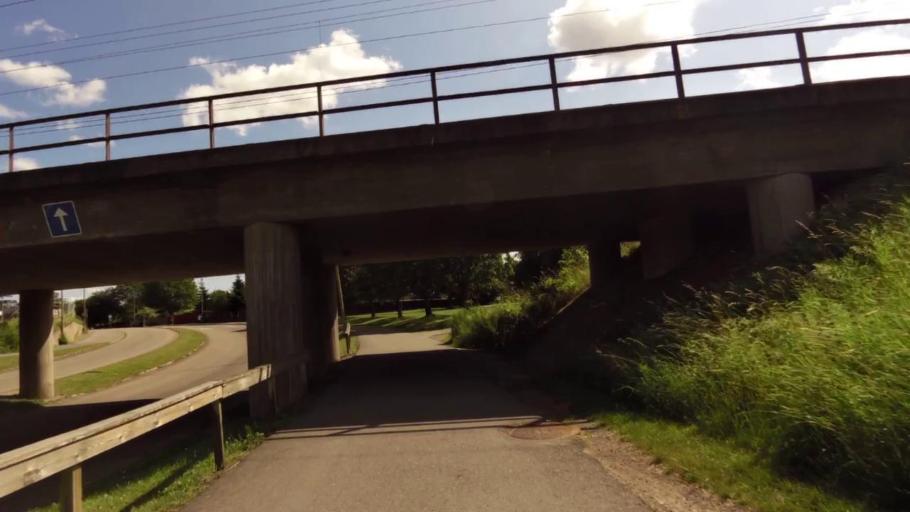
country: SE
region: OEstergoetland
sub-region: Linkopings Kommun
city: Linkoping
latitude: 58.4208
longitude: 15.5865
